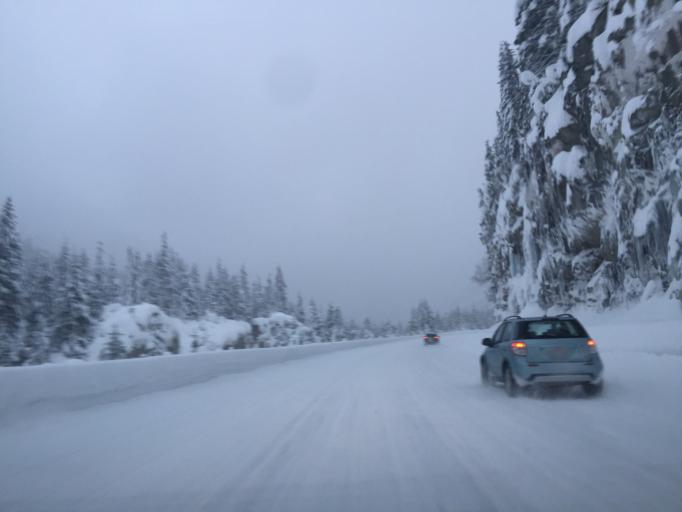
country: US
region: Washington
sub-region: Chelan County
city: Leavenworth
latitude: 47.7838
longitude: -121.0298
